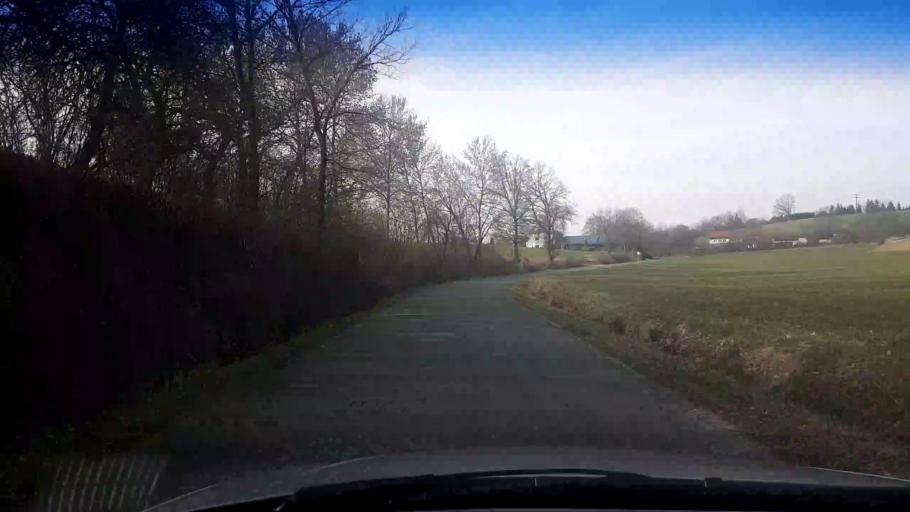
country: DE
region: Bavaria
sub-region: Upper Franconia
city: Burgebrach
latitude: 49.8157
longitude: 10.7501
